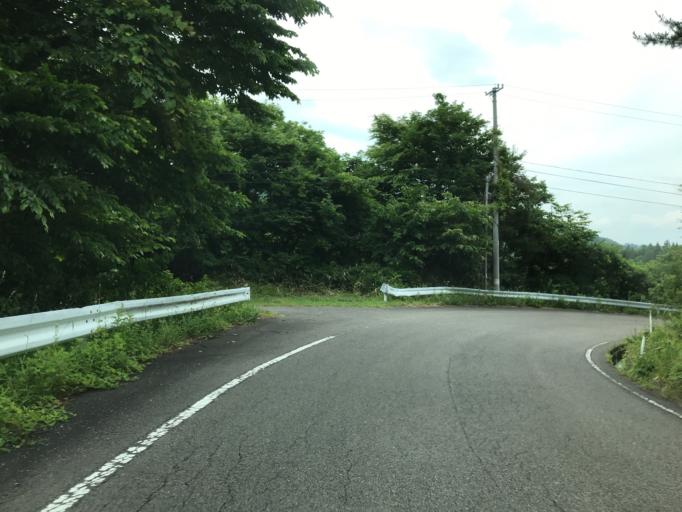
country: JP
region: Fukushima
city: Funehikimachi-funehiki
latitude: 37.4202
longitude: 140.7341
